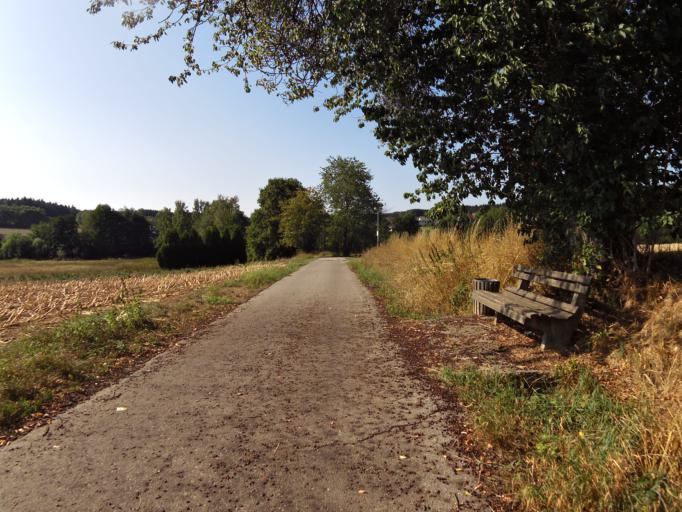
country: DE
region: Baden-Wuerttemberg
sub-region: Karlsruhe Region
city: Mudau
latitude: 49.5178
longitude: 9.2011
